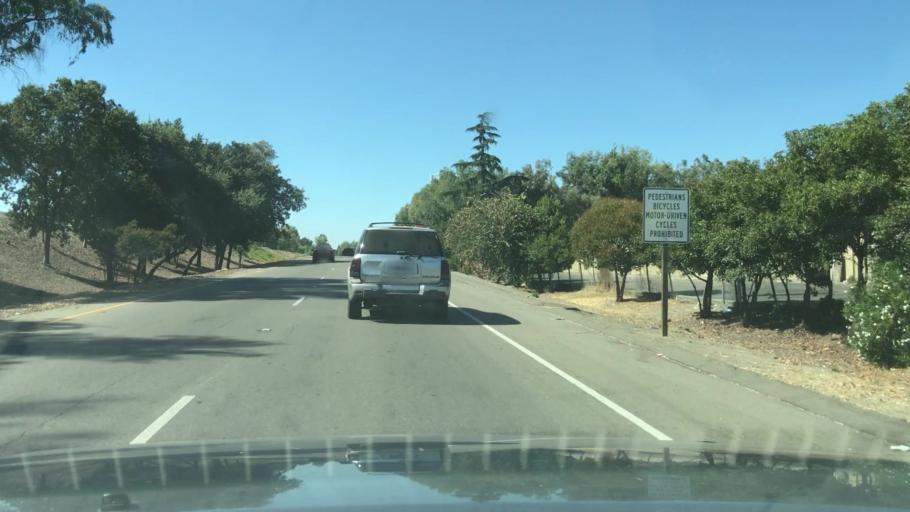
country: US
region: California
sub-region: San Joaquin County
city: Lincoln Village
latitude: 38.0216
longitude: -121.3583
